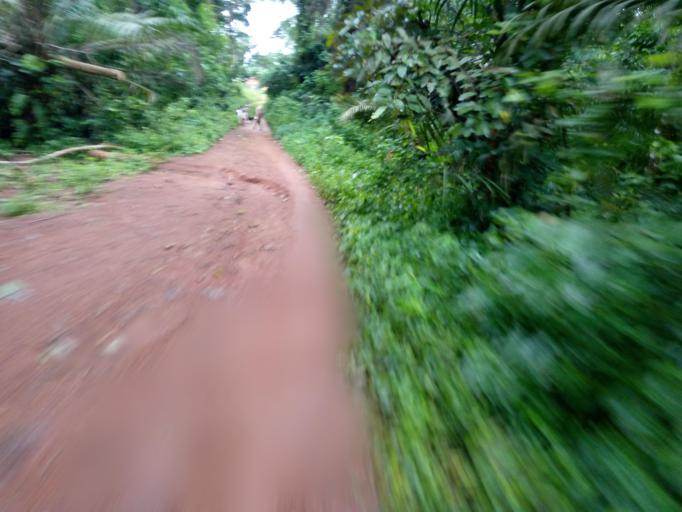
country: SL
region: Eastern Province
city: Buedu
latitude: 8.4701
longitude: -10.3474
